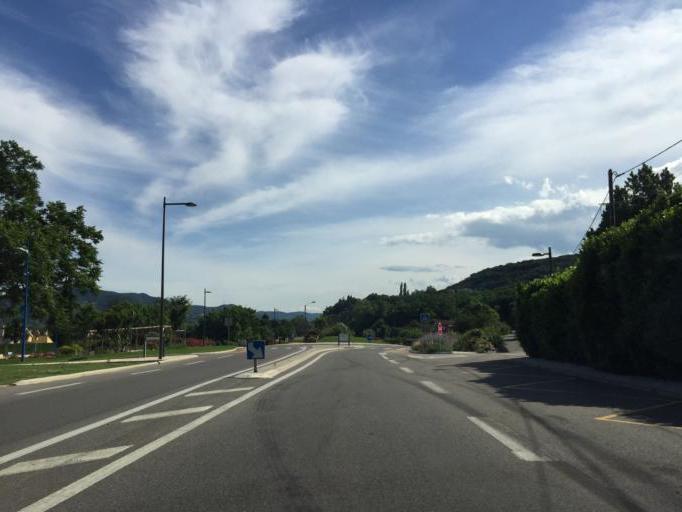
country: FR
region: Rhone-Alpes
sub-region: Departement de l'Ardeche
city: Le Pouzin
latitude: 44.7428
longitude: 4.7436
